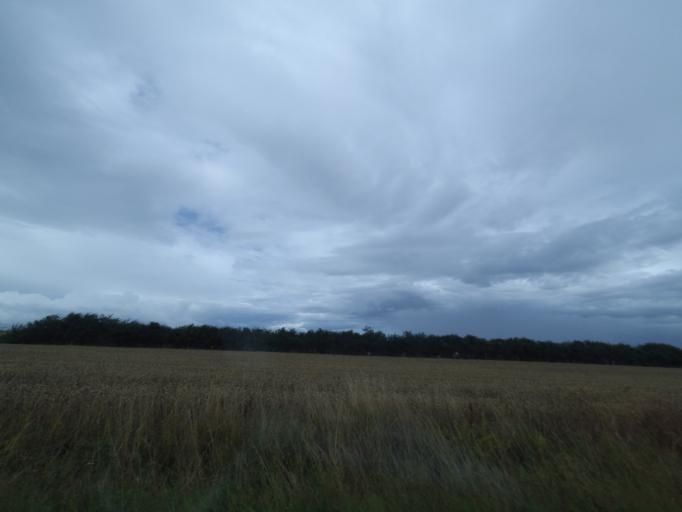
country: DK
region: South Denmark
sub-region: Nordfyns Kommune
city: Sonderso
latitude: 55.4923
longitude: 10.2821
